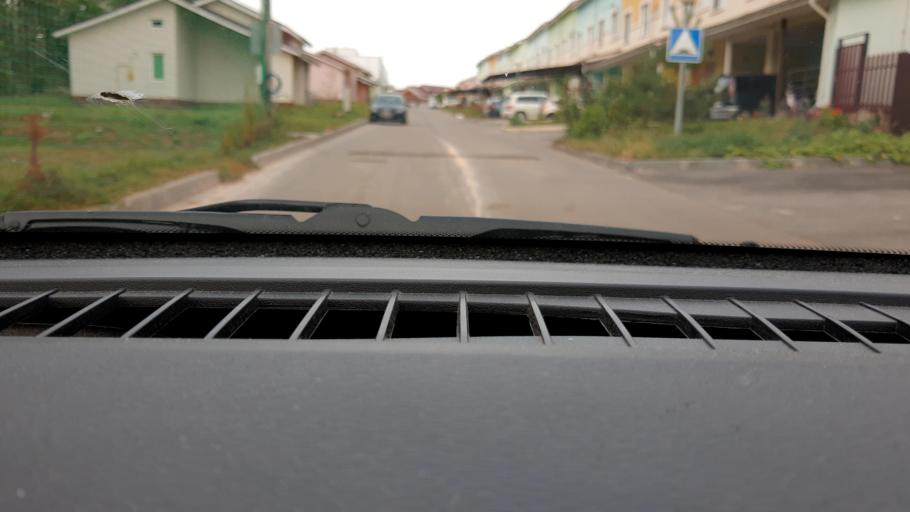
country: RU
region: Nizjnij Novgorod
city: Burevestnik
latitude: 56.0621
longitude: 43.8779
